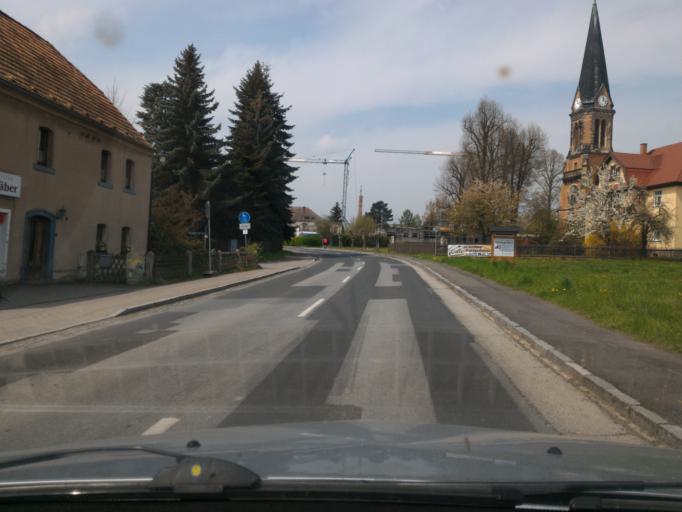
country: DE
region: Saxony
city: Bertsdorf-Hoernitz
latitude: 50.9005
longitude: 14.7515
